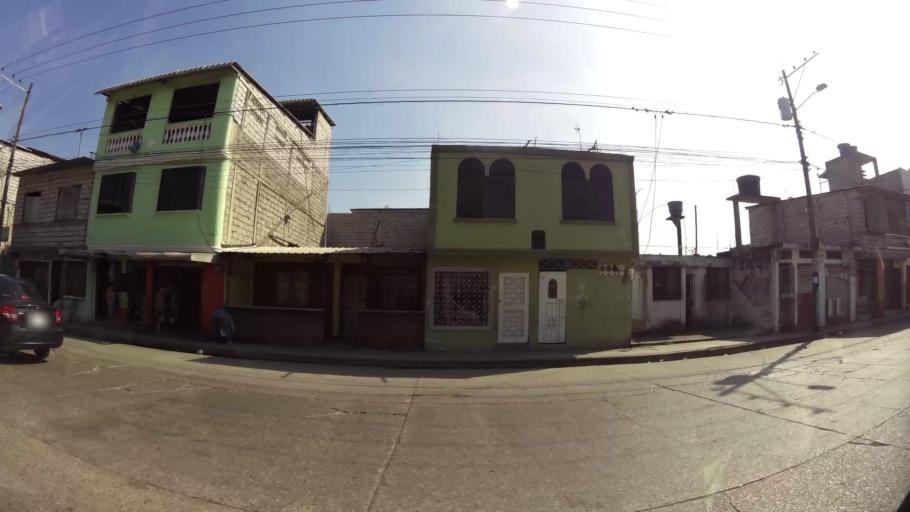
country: EC
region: Guayas
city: Eloy Alfaro
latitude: -2.1688
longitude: -79.8048
